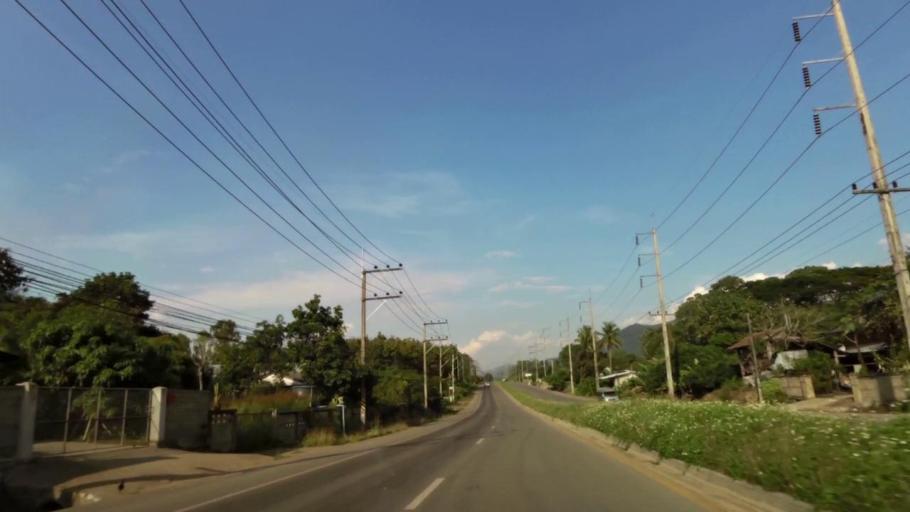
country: TH
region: Chiang Rai
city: Khun Tan
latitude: 19.8727
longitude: 100.2866
